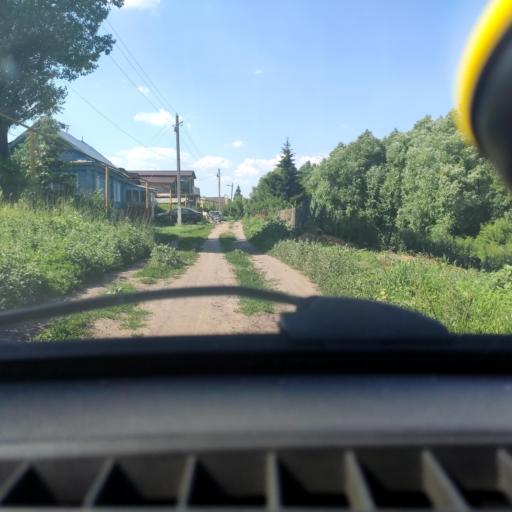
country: RU
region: Samara
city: Povolzhskiy
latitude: 53.7569
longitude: 49.7332
